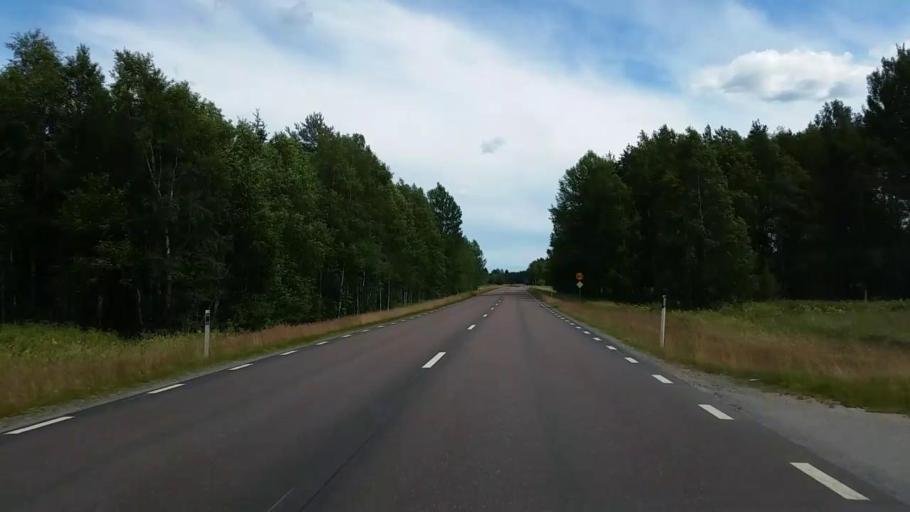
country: SE
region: Gaevleborg
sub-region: Ovanakers Kommun
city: Edsbyn
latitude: 61.3660
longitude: 15.8783
